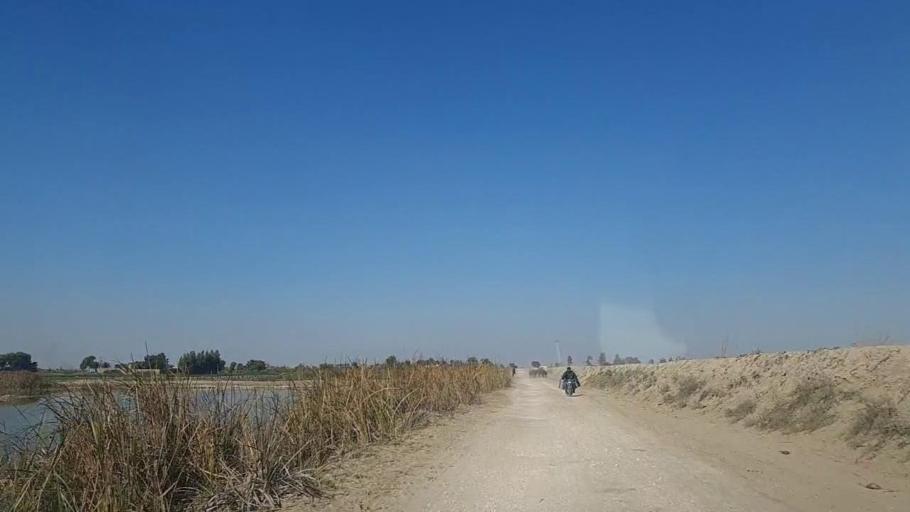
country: PK
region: Sindh
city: Sanghar
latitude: 26.2169
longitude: 68.9291
